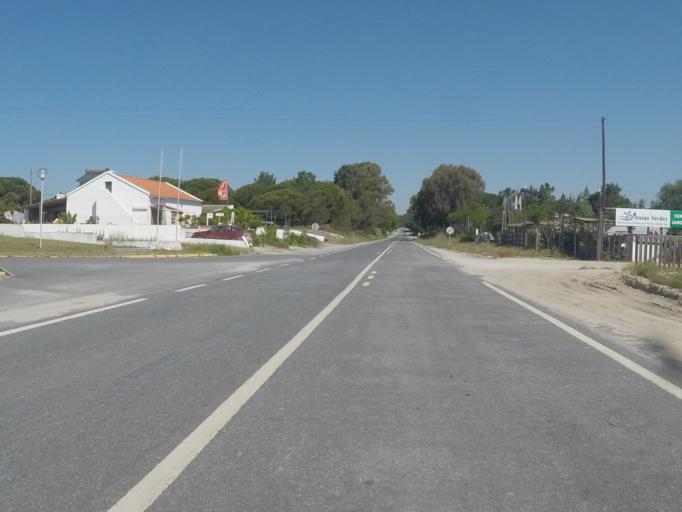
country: PT
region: Setubal
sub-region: Grandola
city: Grandola
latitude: 38.3100
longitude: -8.7427
